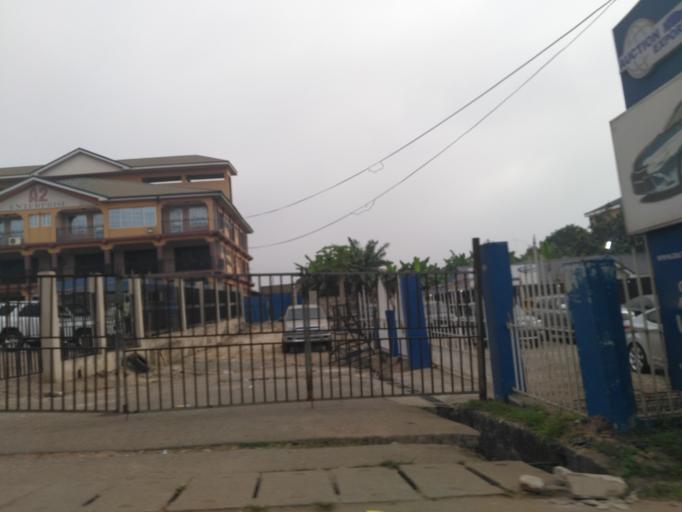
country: GH
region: Ashanti
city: Tafo
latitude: 6.7137
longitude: -1.6027
